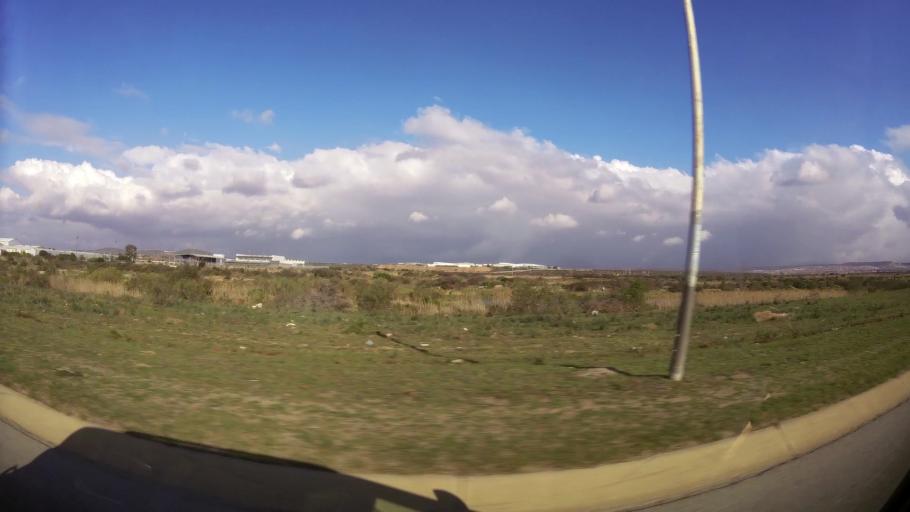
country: ZA
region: Eastern Cape
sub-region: Nelson Mandela Bay Metropolitan Municipality
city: Uitenhage
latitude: -33.7906
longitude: 25.4188
